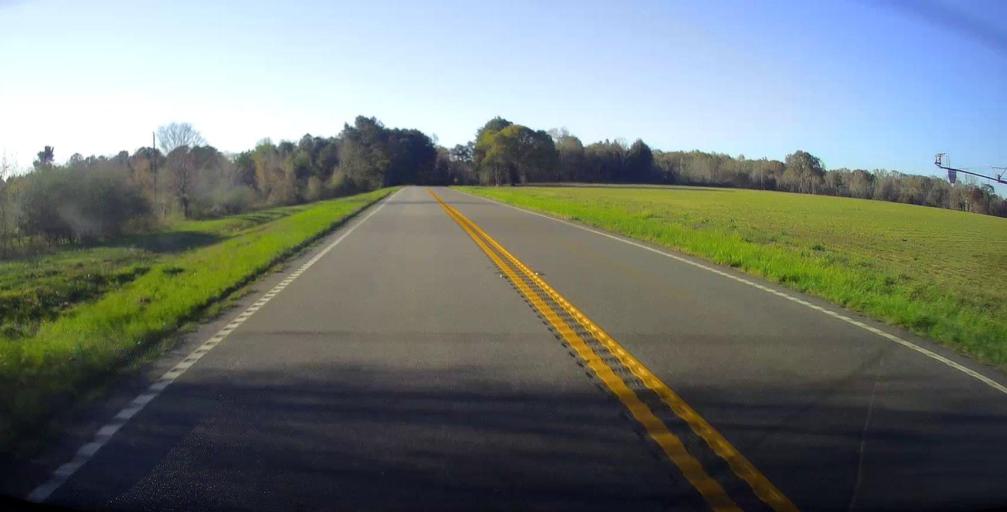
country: US
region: Georgia
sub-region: Pulaski County
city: Hawkinsville
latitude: 32.1887
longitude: -83.3670
